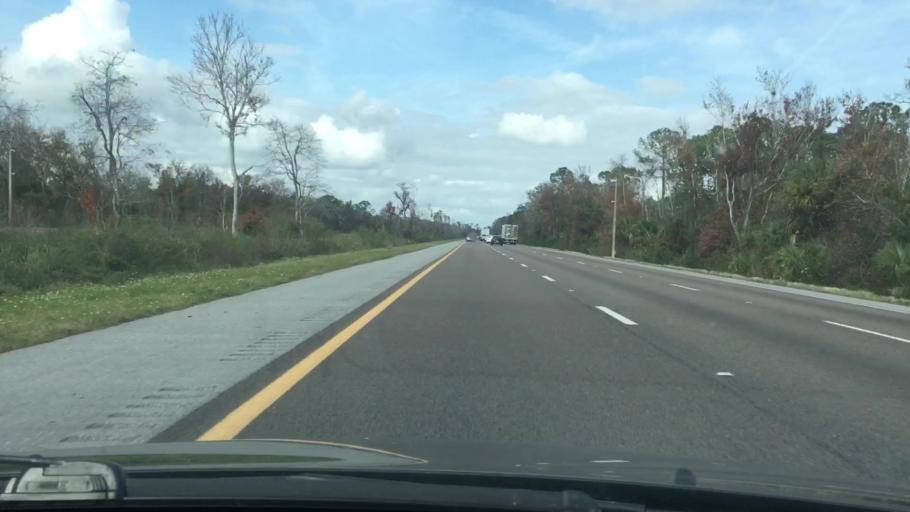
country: US
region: Florida
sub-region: Volusia County
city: Oak Hill
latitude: 28.8944
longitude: -80.9286
